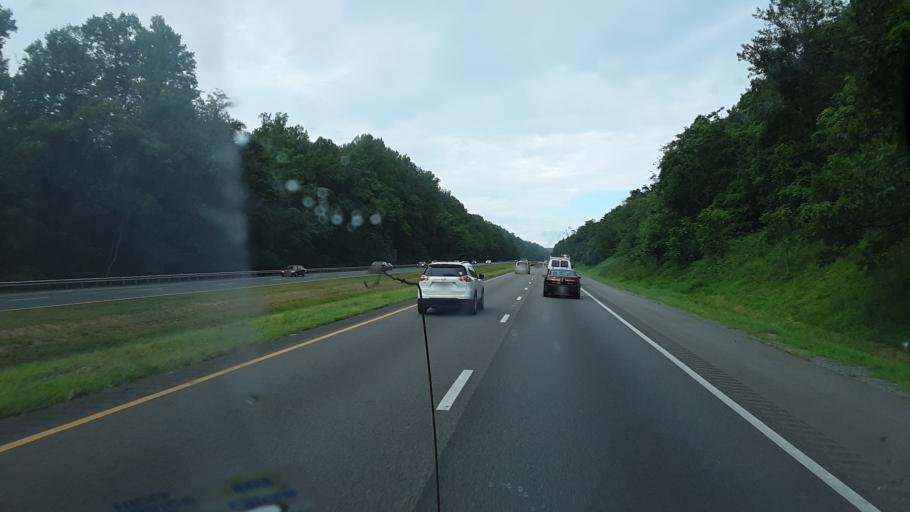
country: US
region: Virginia
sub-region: City of Charlottesville
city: Charlottesville
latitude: 38.0223
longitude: -78.5527
